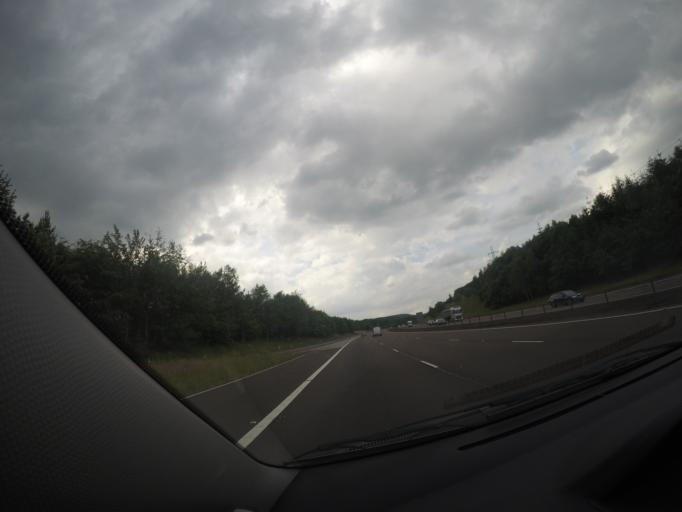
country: GB
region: Scotland
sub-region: Dumfries and Galloway
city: Moffat
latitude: 55.3150
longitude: -3.4585
